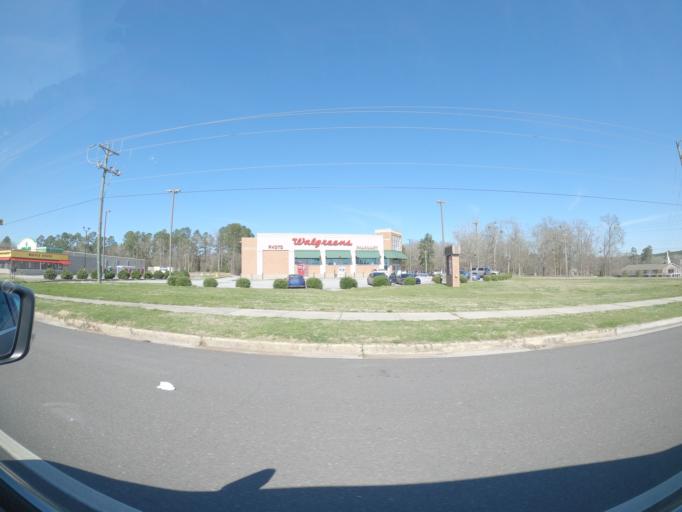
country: US
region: South Carolina
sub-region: Aiken County
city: Clearwater
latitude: 33.5044
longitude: -81.8991
